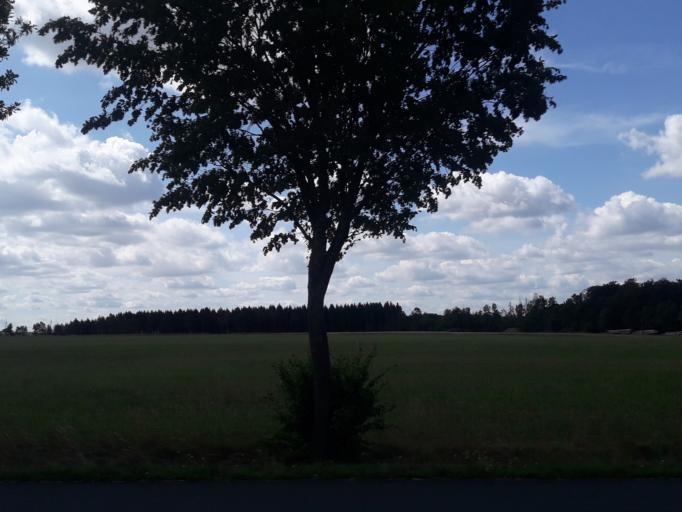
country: DE
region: North Rhine-Westphalia
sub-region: Regierungsbezirk Detmold
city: Paderborn
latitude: 51.6870
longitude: 8.8048
